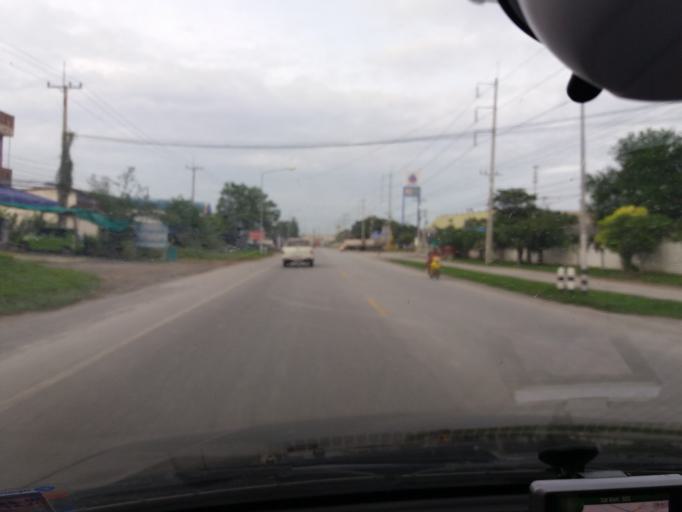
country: TH
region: Suphan Buri
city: U Thong
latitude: 14.4077
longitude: 99.8988
